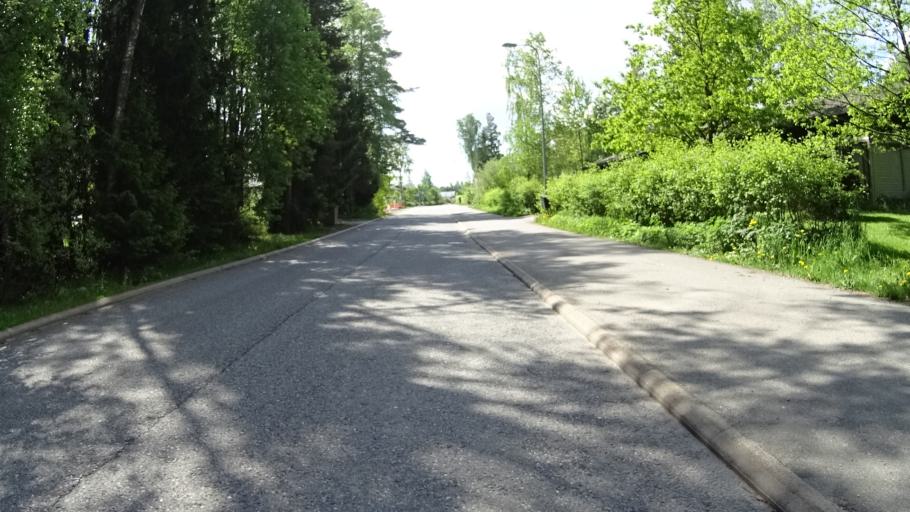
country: FI
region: Uusimaa
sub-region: Helsinki
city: Espoo
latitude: 60.2250
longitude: 24.6406
